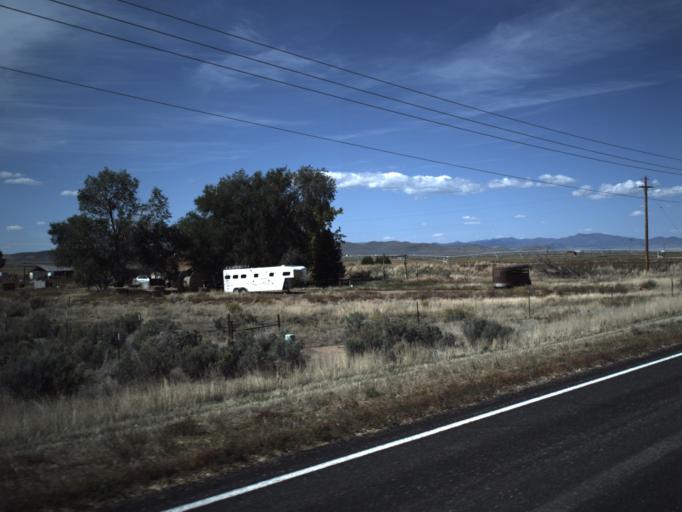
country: US
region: Utah
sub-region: Washington County
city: Enterprise
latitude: 37.6176
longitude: -113.6612
